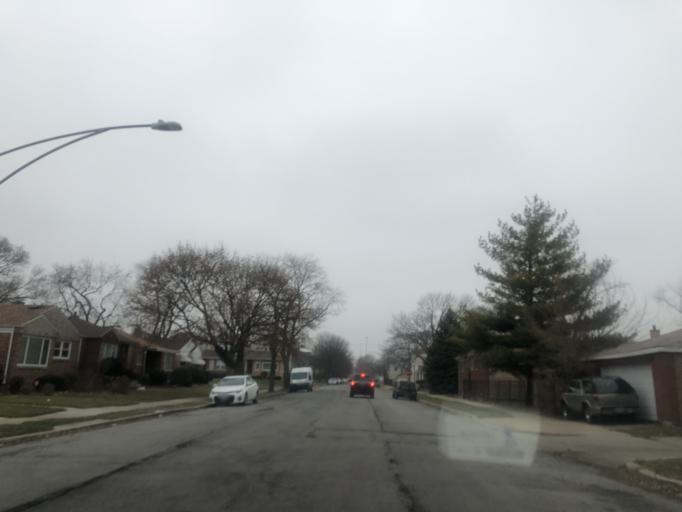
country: US
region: Illinois
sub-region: Cook County
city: Calumet Park
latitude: 41.7328
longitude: -87.6182
